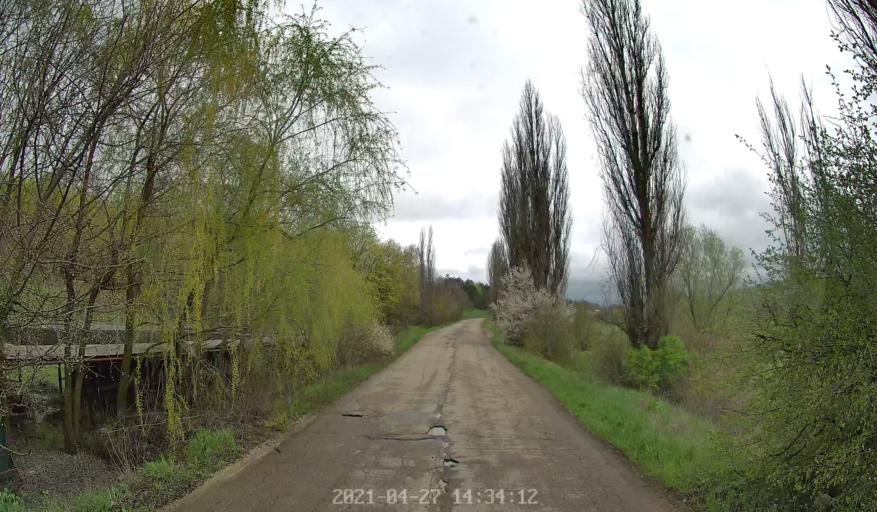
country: MD
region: Chisinau
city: Vadul lui Voda
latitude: 47.0576
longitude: 29.0276
